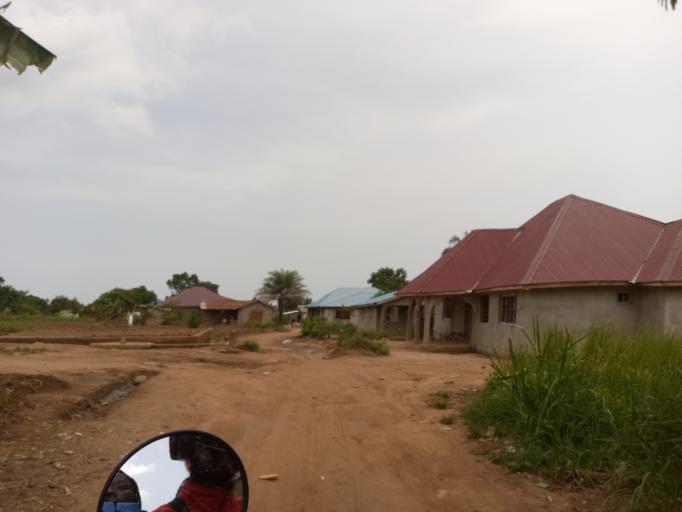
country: SL
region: Western Area
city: Waterloo
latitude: 8.3338
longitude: -13.0241
